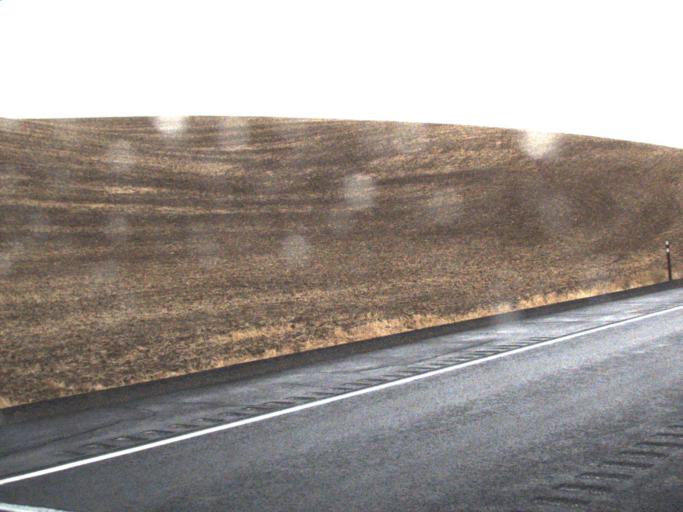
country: US
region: Washington
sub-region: Whitman County
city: Colfax
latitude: 46.8159
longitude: -117.3221
